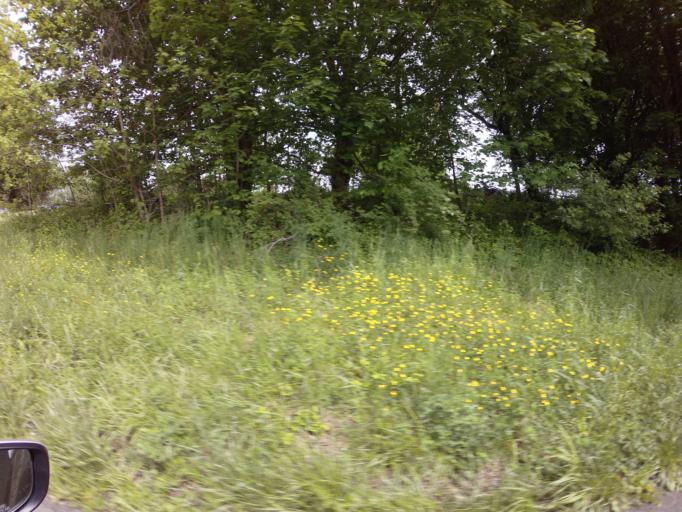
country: US
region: Maryland
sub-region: Carroll County
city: New Windsor
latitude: 39.4752
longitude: -77.0331
